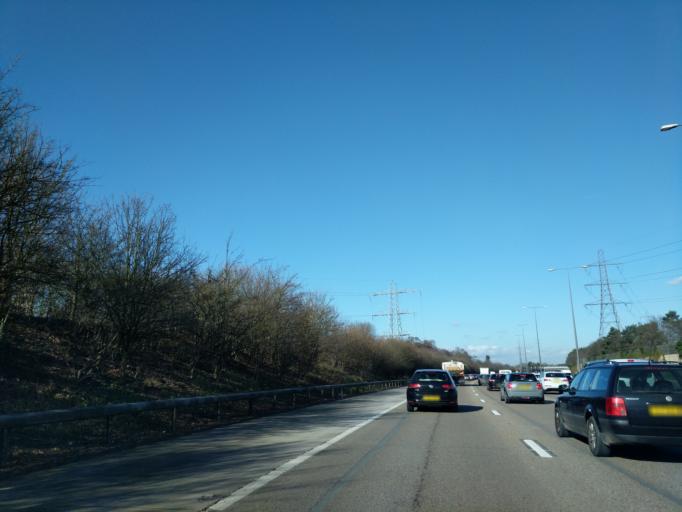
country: GB
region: England
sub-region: Surrey
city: Byfleet
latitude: 51.3332
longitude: -0.4828
